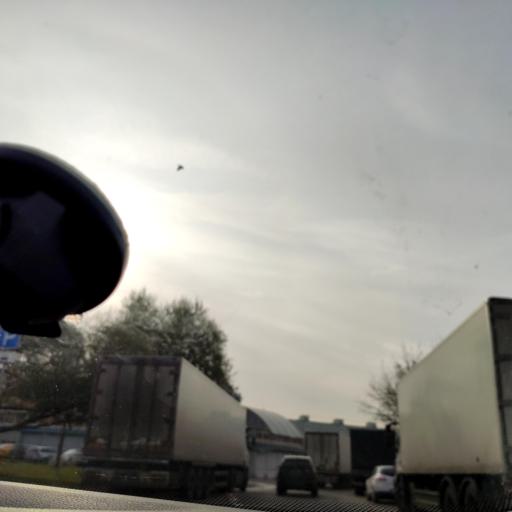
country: RU
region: Moskovskaya
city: Vostochnoe Degunino
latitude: 55.8840
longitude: 37.5529
